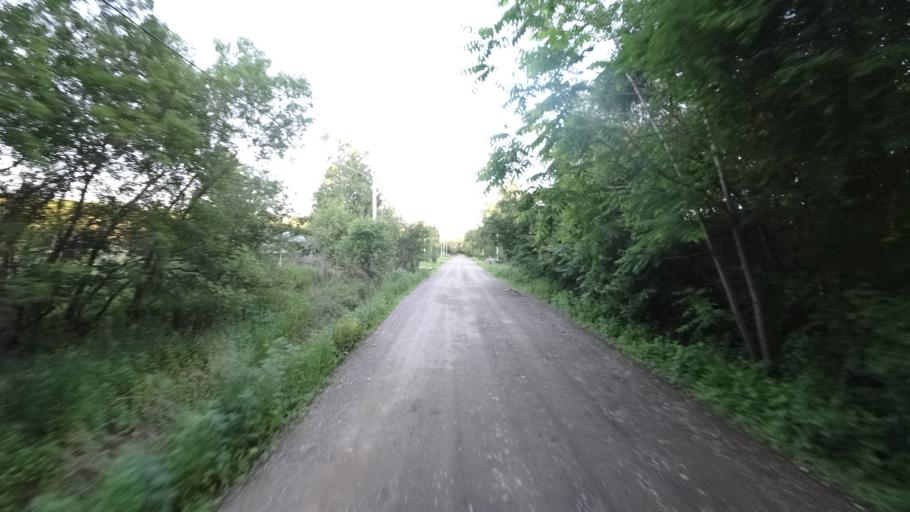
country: RU
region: Khabarovsk Krai
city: Khor
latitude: 47.8524
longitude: 134.9829
